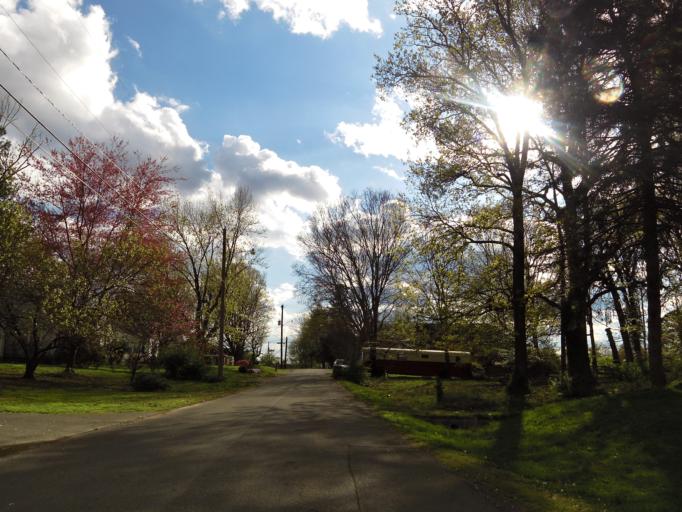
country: US
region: Tennessee
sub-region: Blount County
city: Maryville
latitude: 35.7650
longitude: -83.9582
